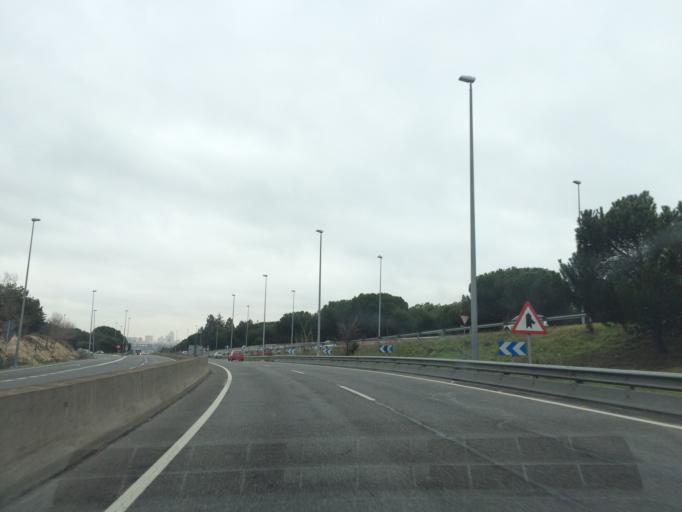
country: ES
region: Madrid
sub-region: Provincia de Madrid
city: Moncloa-Aravaca
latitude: 40.4497
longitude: -3.7629
